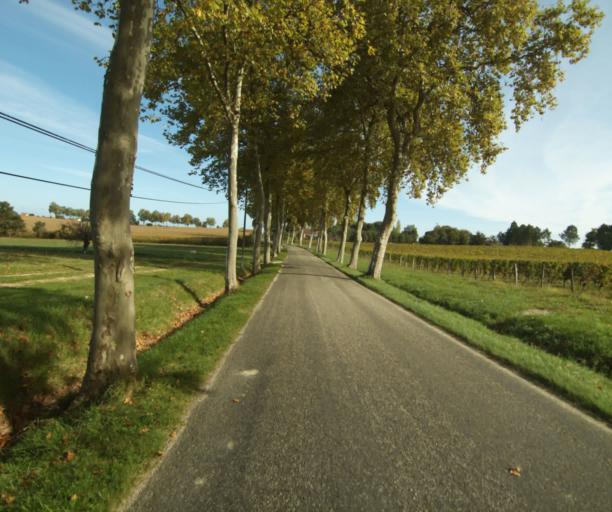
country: FR
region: Midi-Pyrenees
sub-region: Departement du Gers
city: Eauze
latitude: 43.9388
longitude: 0.0955
